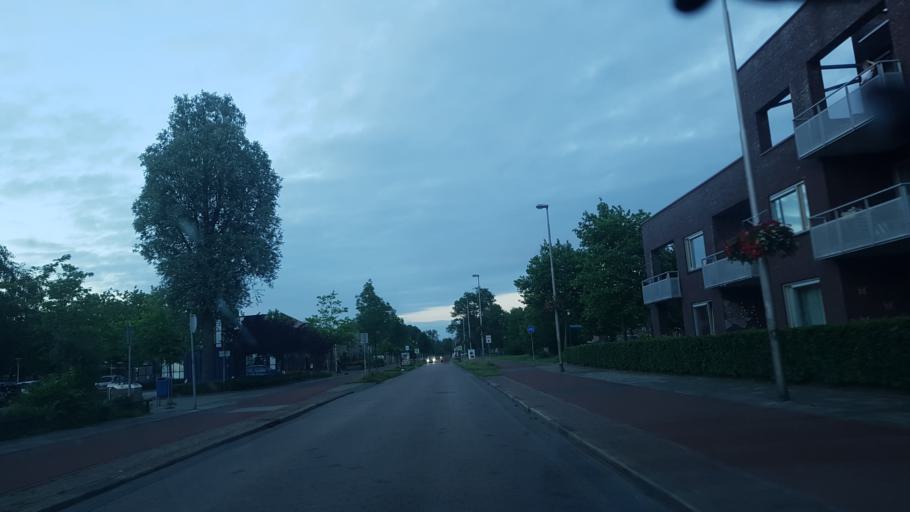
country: NL
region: Friesland
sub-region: Gemeente Leeuwarden
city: Leeuwarden
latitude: 53.2079
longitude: 5.8201
